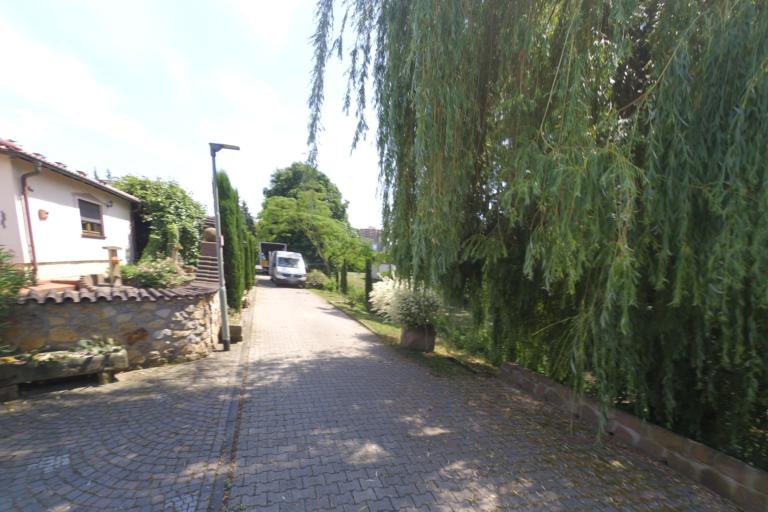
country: DE
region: Rheinland-Pfalz
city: Neuhofen
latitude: 49.4194
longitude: 8.4194
